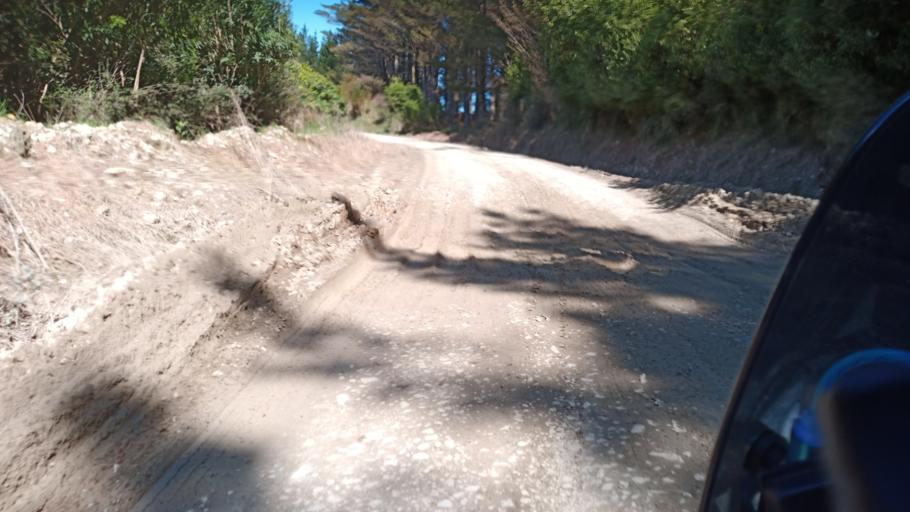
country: NZ
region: Gisborne
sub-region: Gisborne District
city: Gisborne
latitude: -38.9035
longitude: 177.8037
